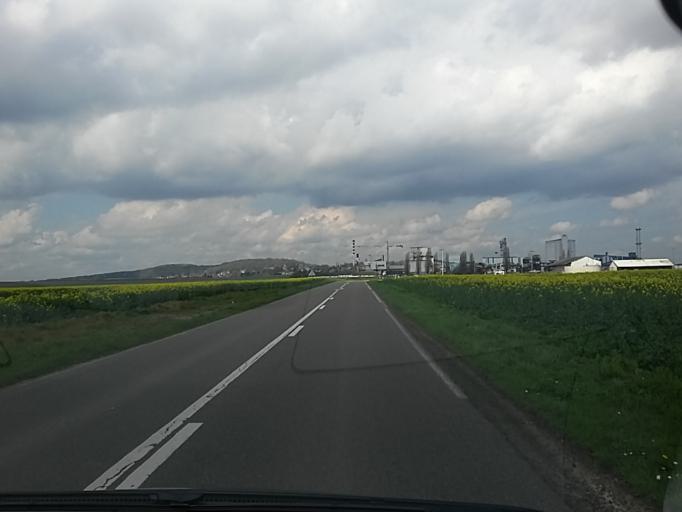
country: FR
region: Picardie
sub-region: Departement de l'Oise
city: Chevrieres
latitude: 49.3542
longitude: 2.6725
